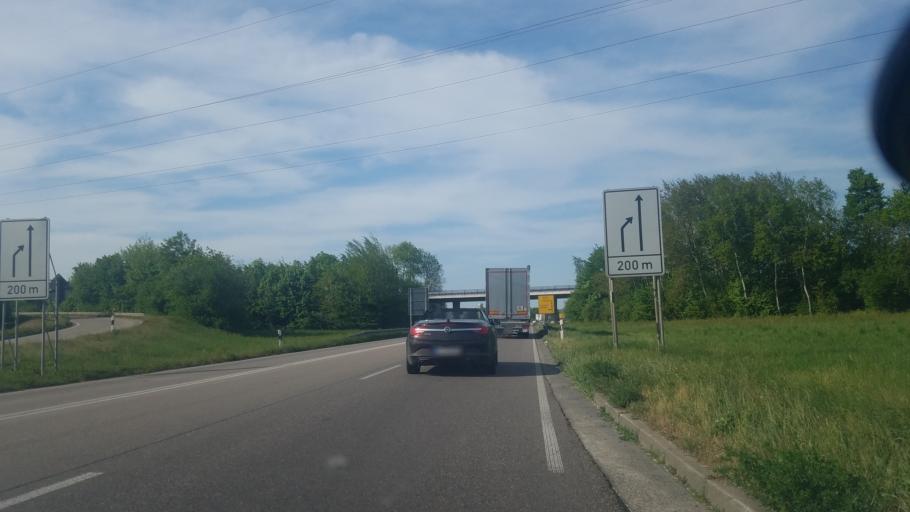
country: DE
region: Baden-Wuerttemberg
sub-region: Freiburg Region
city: Kehl
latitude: 48.5798
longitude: 7.8271
